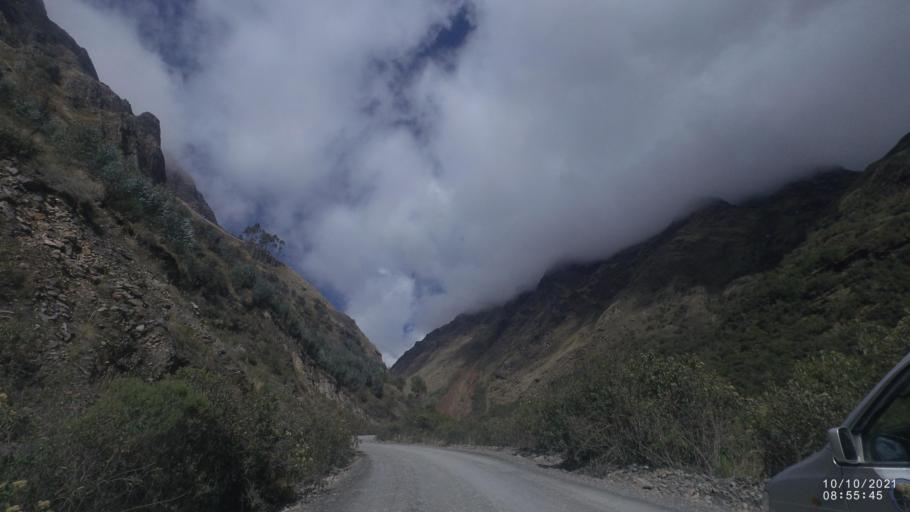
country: BO
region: La Paz
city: Quime
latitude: -16.9879
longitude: -67.2401
